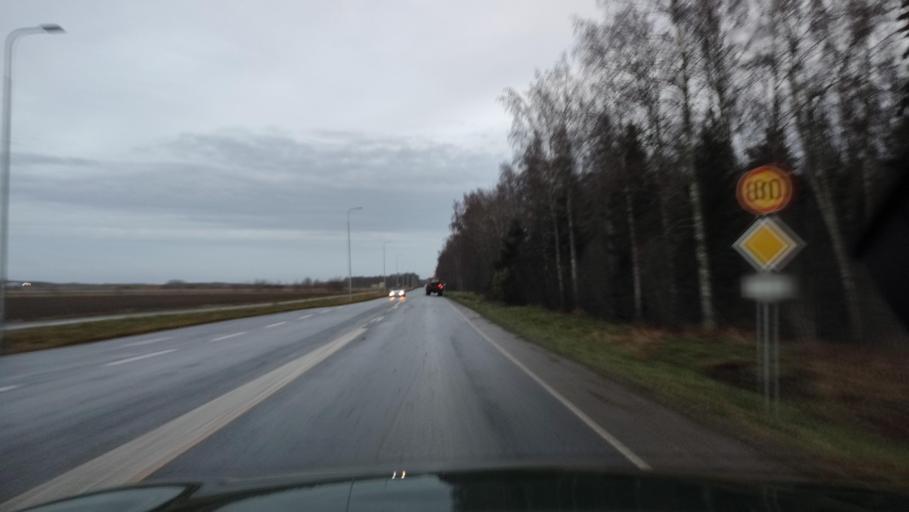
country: FI
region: Ostrobothnia
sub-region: Vaasa
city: Ristinummi
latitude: 63.0475
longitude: 21.7304
